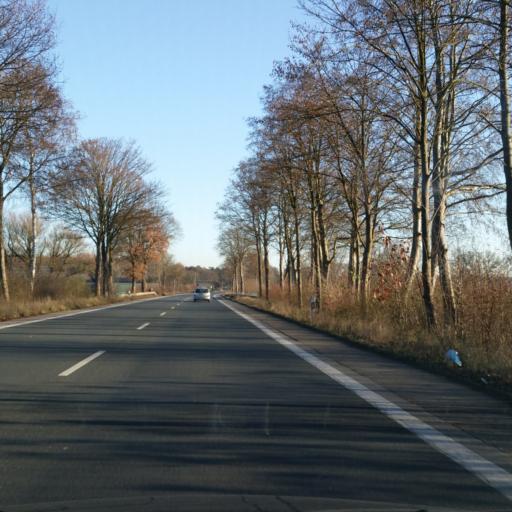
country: DE
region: North Rhine-Westphalia
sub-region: Regierungsbezirk Munster
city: Isselburg
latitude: 51.8193
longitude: 6.4624
